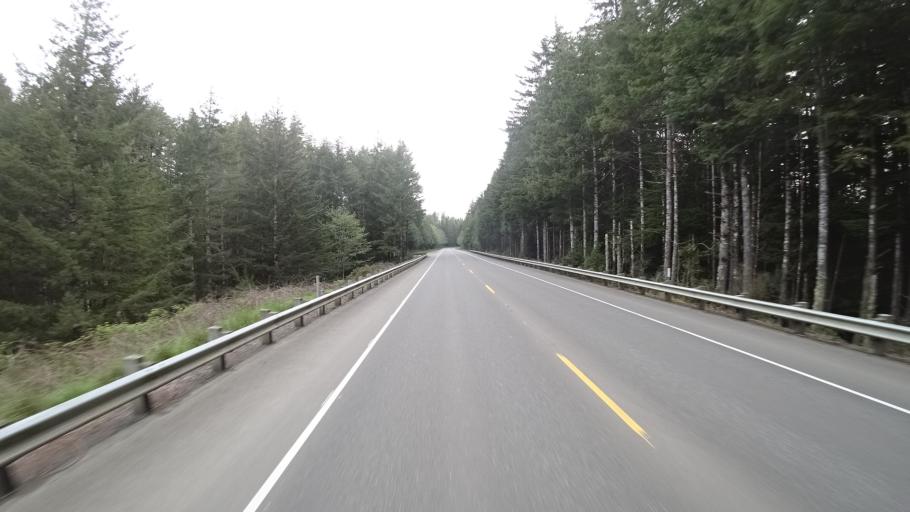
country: US
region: Oregon
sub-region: Coos County
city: Barview
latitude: 43.2500
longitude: -124.2866
